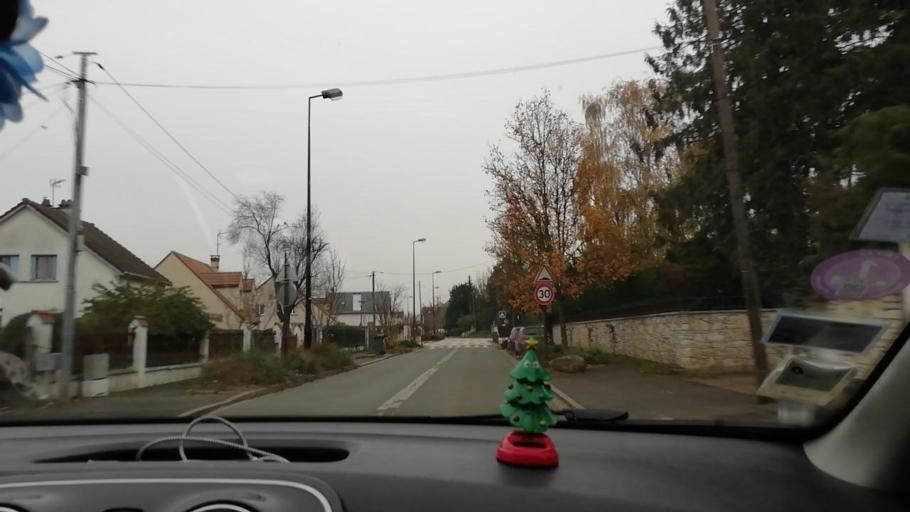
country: FR
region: Ile-de-France
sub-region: Departement de Seine-et-Marne
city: Claye-Souilly
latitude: 48.9526
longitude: 2.6707
